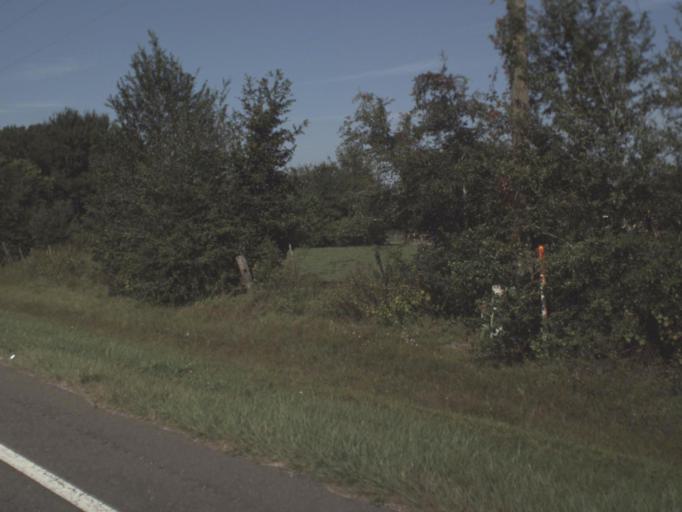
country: US
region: Florida
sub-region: Hardee County
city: Wauchula
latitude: 27.5515
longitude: -81.7183
